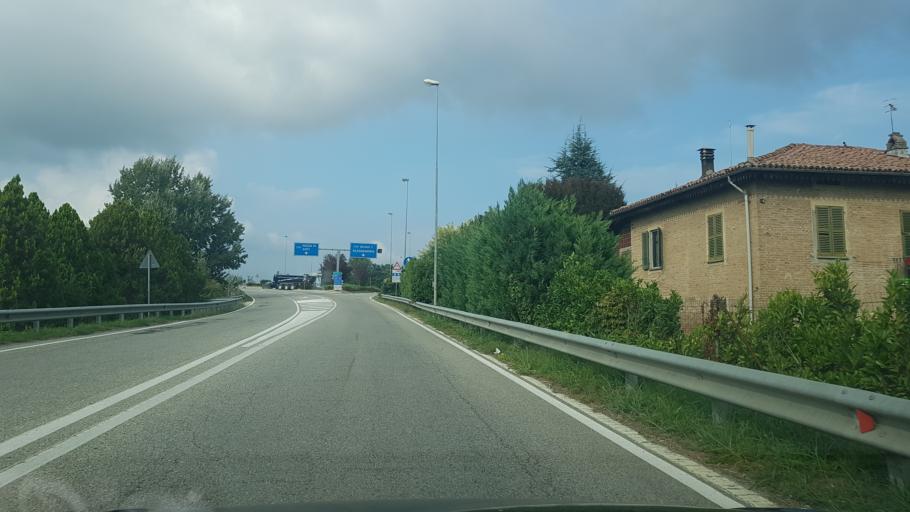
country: IT
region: Piedmont
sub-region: Provincia di Asti
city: Nizza Monferrato
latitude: 44.7660
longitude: 8.3537
